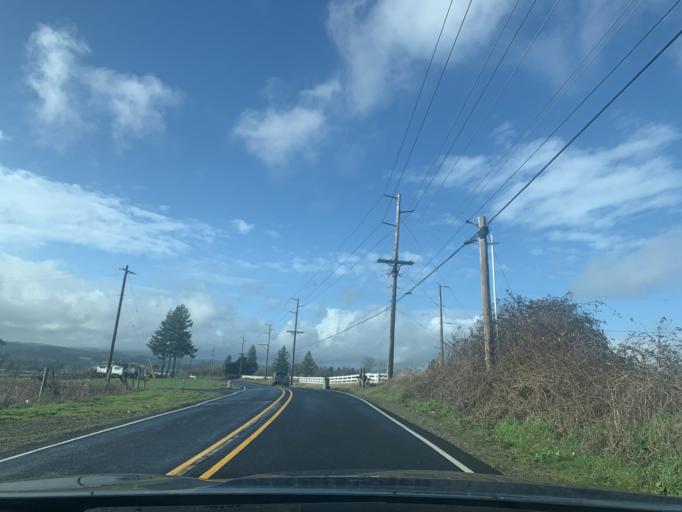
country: US
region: Oregon
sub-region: Washington County
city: King City
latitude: 45.4018
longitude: -122.8358
